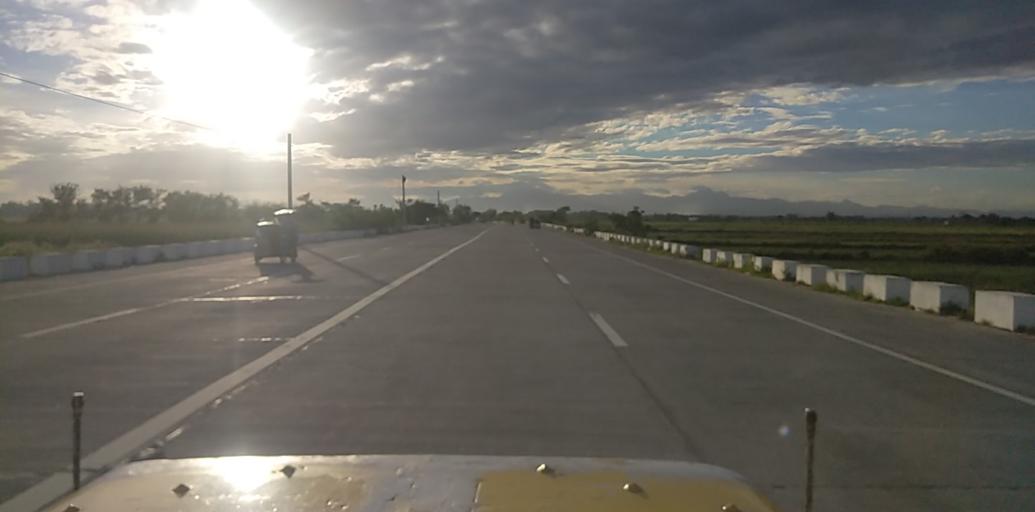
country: PH
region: Central Luzon
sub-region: Province of Pampanga
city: Anao
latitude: 15.1358
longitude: 120.6875
